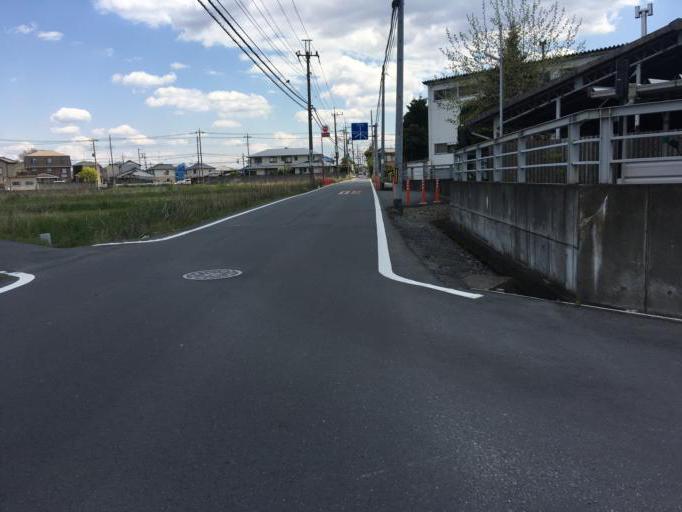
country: JP
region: Saitama
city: Kawagoe
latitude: 35.9331
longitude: 139.4726
